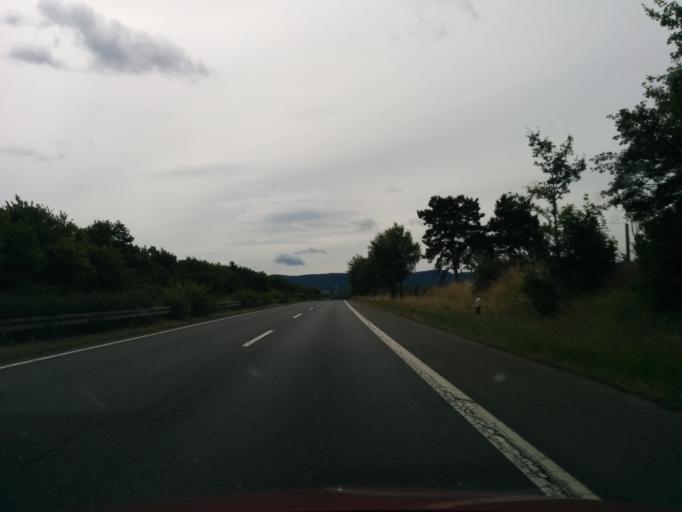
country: DE
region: Lower Saxony
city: Vienenburg
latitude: 51.9218
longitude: 10.5148
